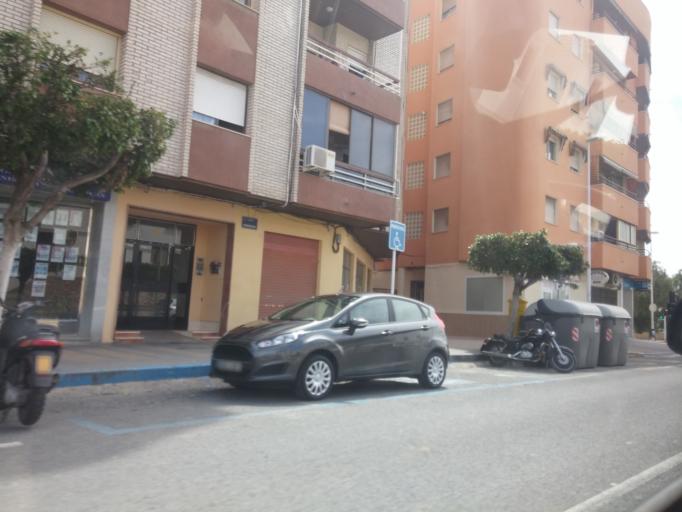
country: ES
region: Valencia
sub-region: Provincia de Alicante
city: Villajoyosa
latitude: 38.5047
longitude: -0.2373
